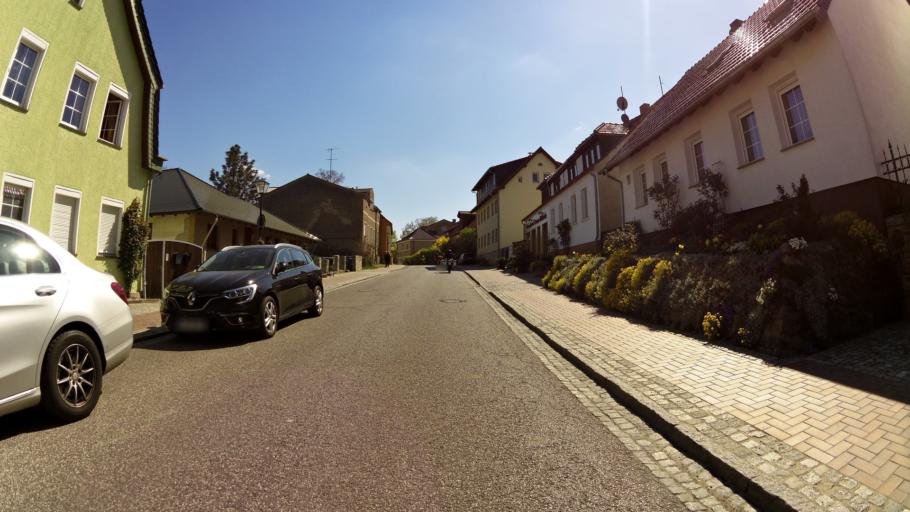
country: DE
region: Brandenburg
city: Buckow
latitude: 52.5650
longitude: 14.0744
